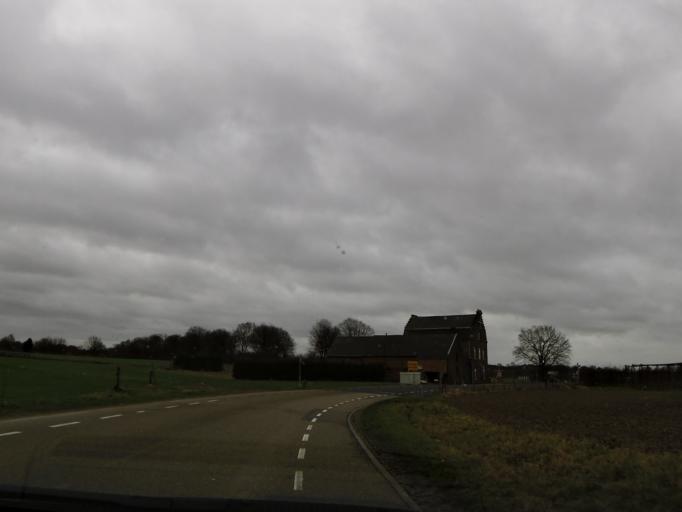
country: NL
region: Limburg
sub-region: Eijsden-Margraten
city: Margraten
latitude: 50.8322
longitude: 5.8210
